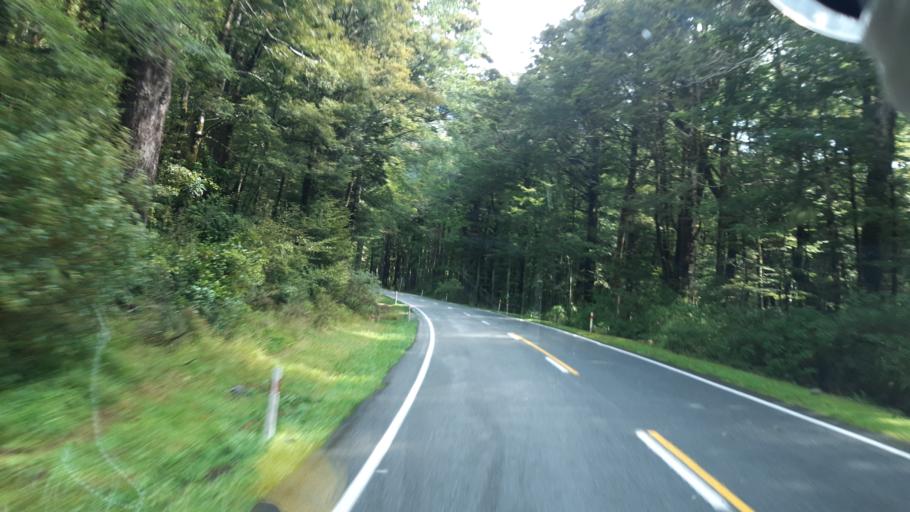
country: NZ
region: Canterbury
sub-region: Hurunui District
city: Amberley
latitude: -42.3807
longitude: 172.3049
